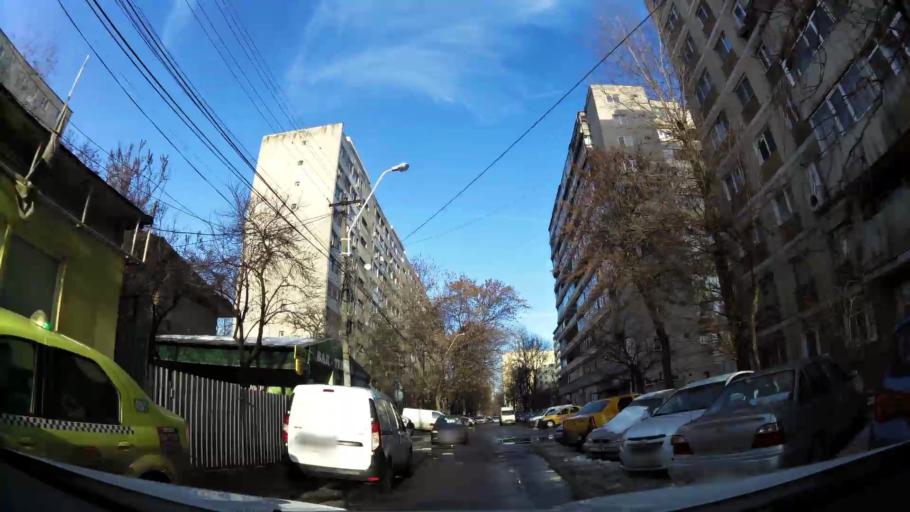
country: RO
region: Bucuresti
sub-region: Municipiul Bucuresti
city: Bucuresti
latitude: 44.3845
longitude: 26.0818
